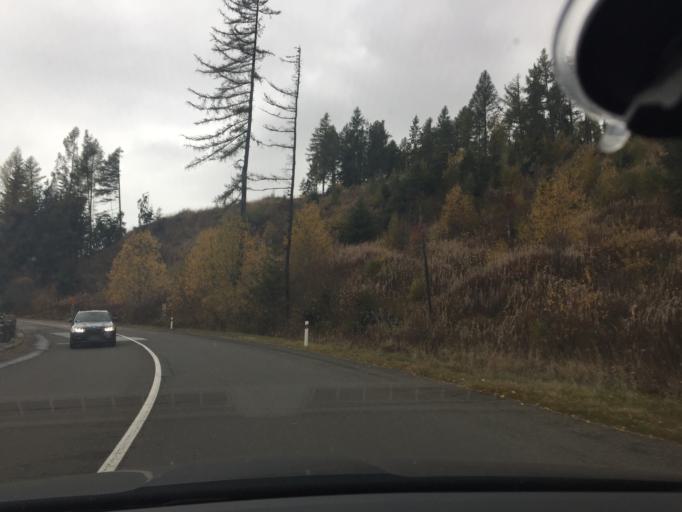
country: SK
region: Presovsky
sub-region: Okres Poprad
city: Strba
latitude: 49.1179
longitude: 20.1101
